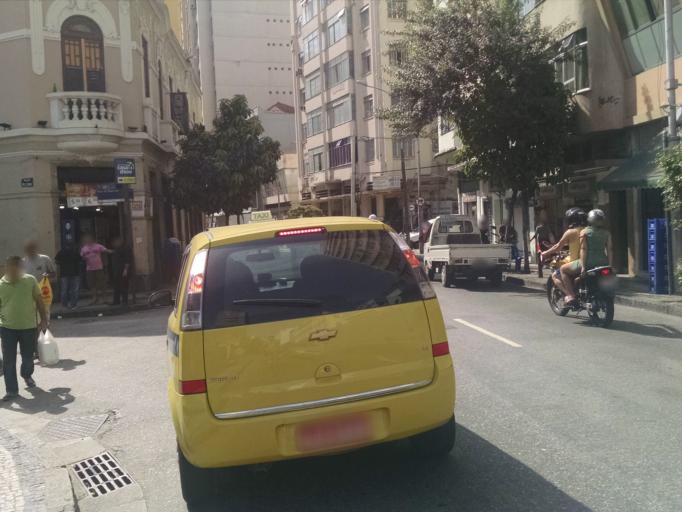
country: BR
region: Rio de Janeiro
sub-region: Rio De Janeiro
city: Rio de Janeiro
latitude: -22.9143
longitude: -43.1898
